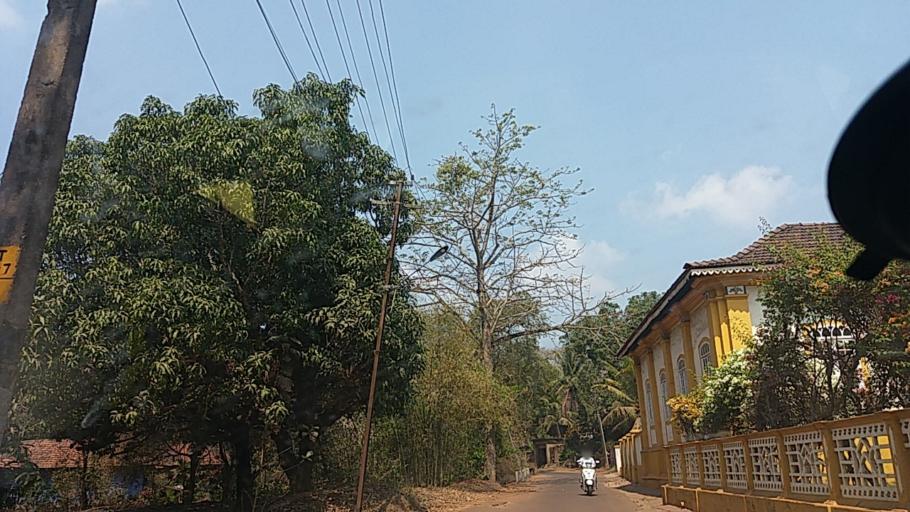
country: IN
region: Goa
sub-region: South Goa
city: Sancoale
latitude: 15.3738
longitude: 73.9152
